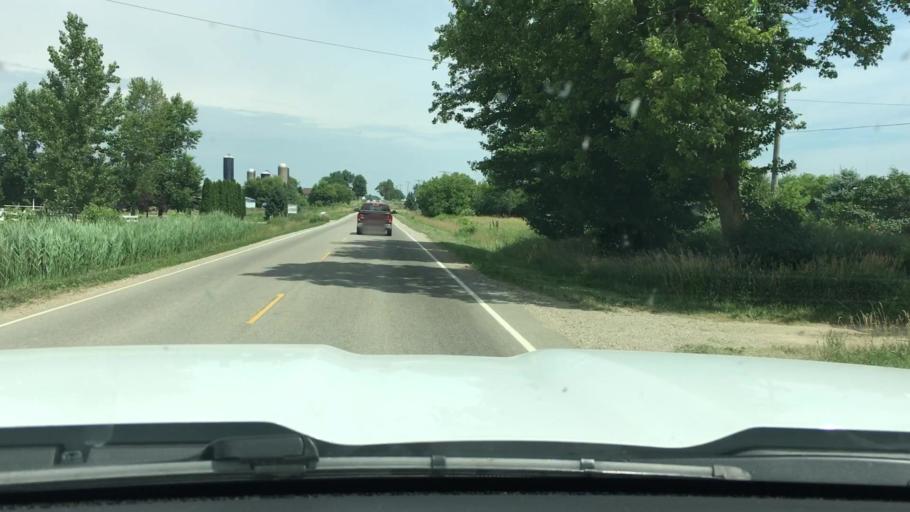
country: US
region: Michigan
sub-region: Sanilac County
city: Brown City
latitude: 43.2714
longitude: -82.9823
